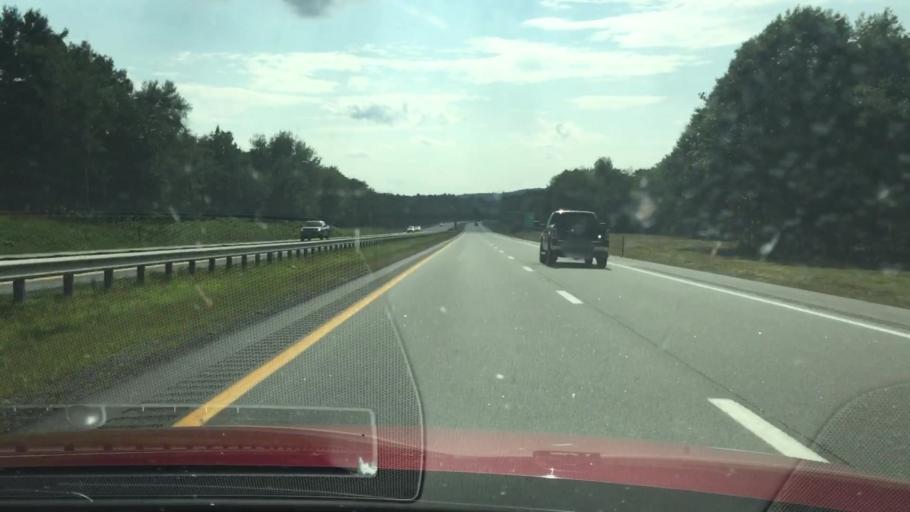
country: US
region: Maine
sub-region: Androscoggin County
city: Lisbon
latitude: 44.0724
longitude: -70.1354
